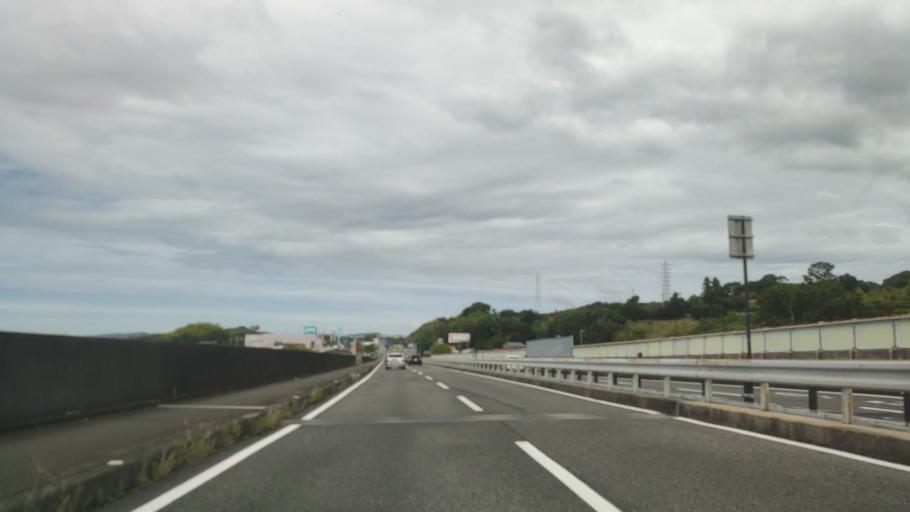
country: JP
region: Wakayama
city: Tanabe
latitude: 33.7179
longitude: 135.4074
